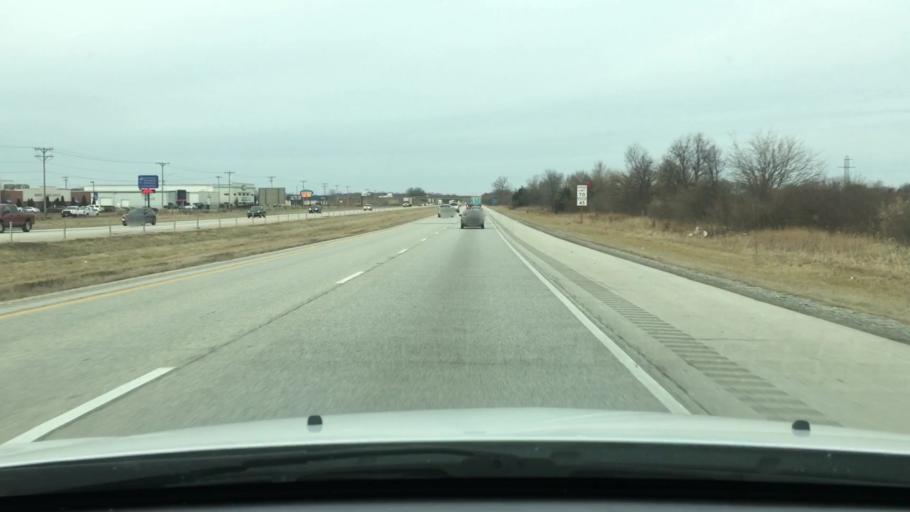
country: US
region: Illinois
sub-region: Sangamon County
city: Grandview
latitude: 39.8392
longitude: -89.5936
